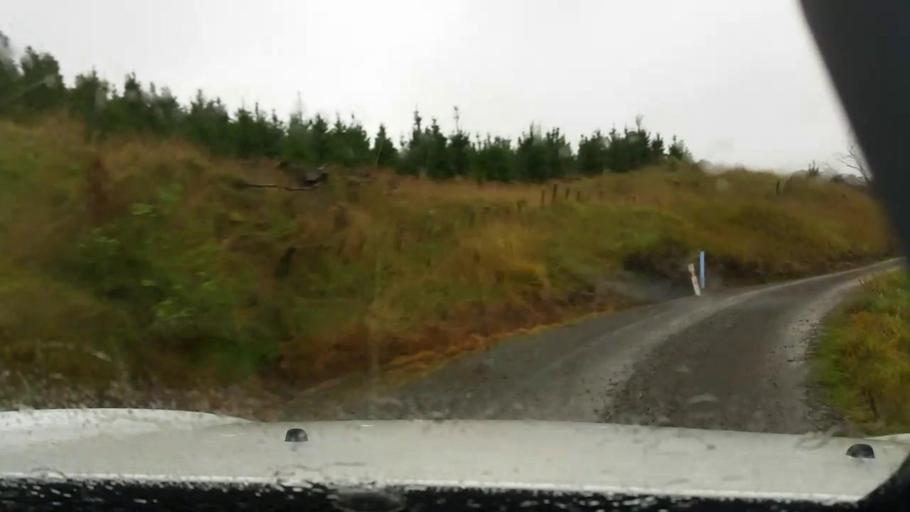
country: NZ
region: Wellington
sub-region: Masterton District
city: Masterton
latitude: -41.1988
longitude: 175.8115
